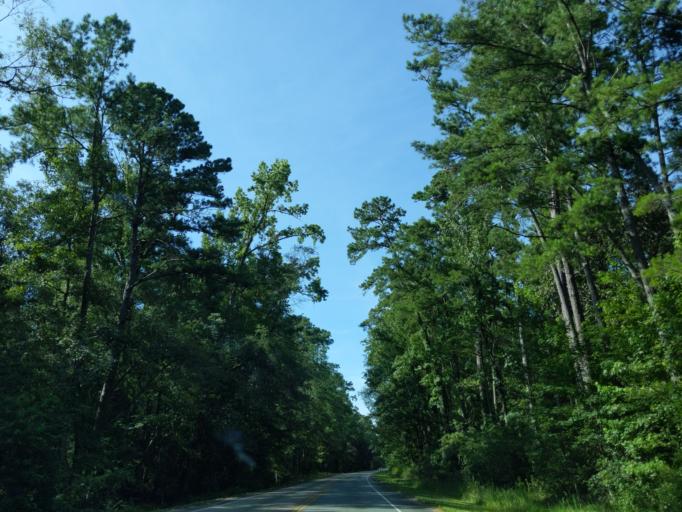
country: US
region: Florida
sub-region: Wakulla County
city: Crawfordville
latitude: 30.2453
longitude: -84.3130
